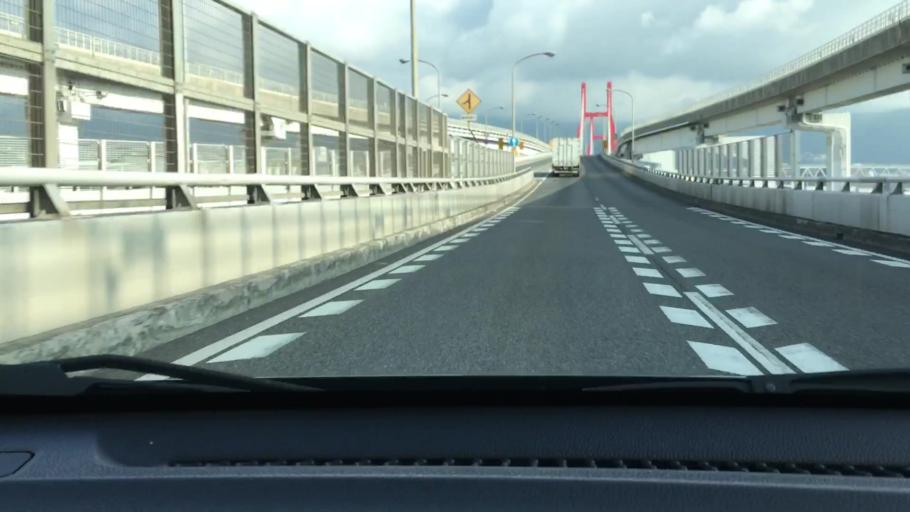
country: JP
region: Hyogo
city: Ashiya
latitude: 34.6943
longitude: 135.2686
